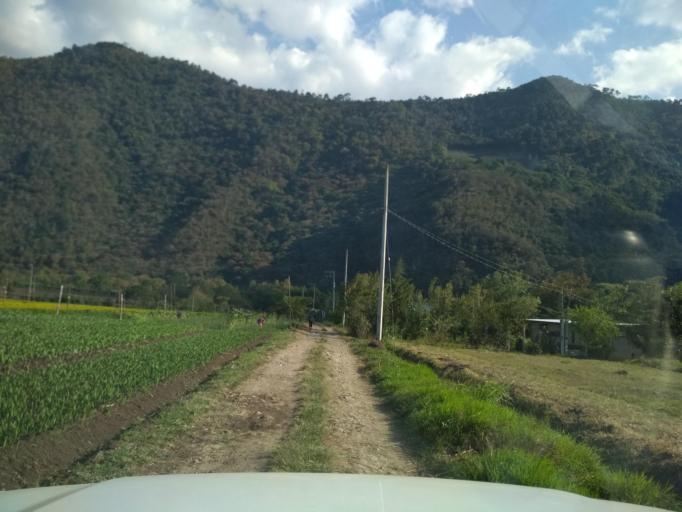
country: MX
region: Veracruz
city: Jalapilla
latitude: 18.8086
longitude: -97.0876
